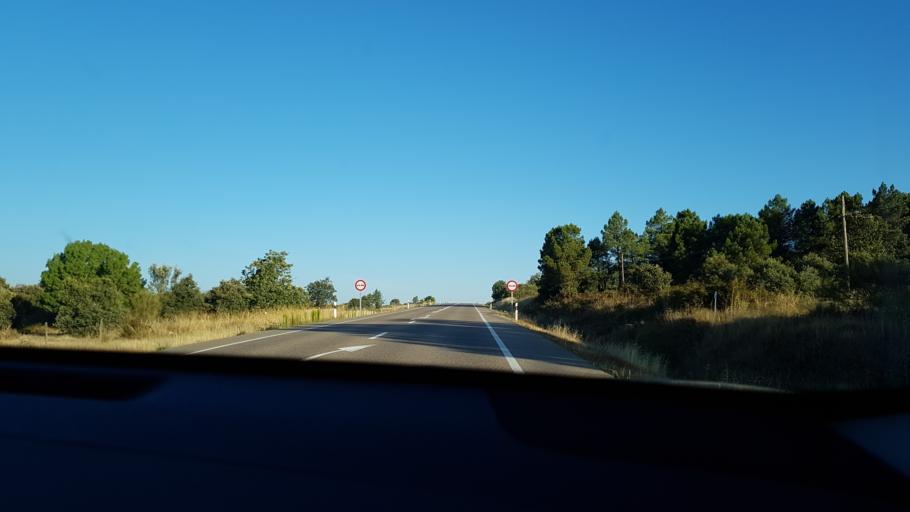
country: ES
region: Castille and Leon
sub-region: Provincia de Zamora
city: Samir de los Canos
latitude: 41.6500
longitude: -6.1709
